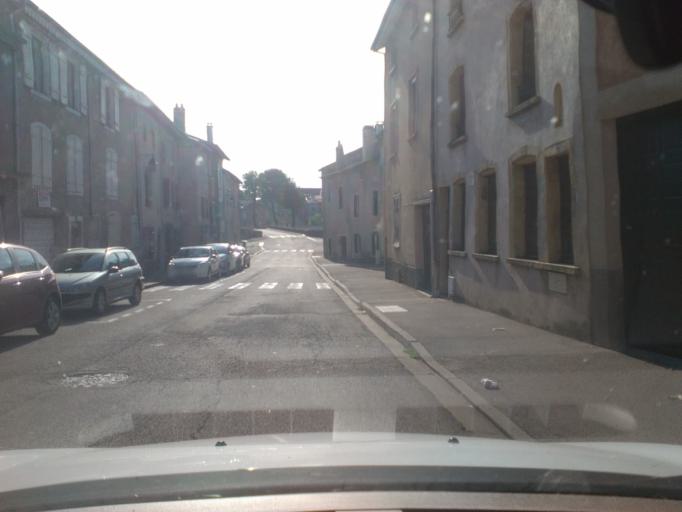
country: FR
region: Lorraine
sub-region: Departement des Vosges
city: Mirecourt
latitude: 48.3005
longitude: 6.1389
